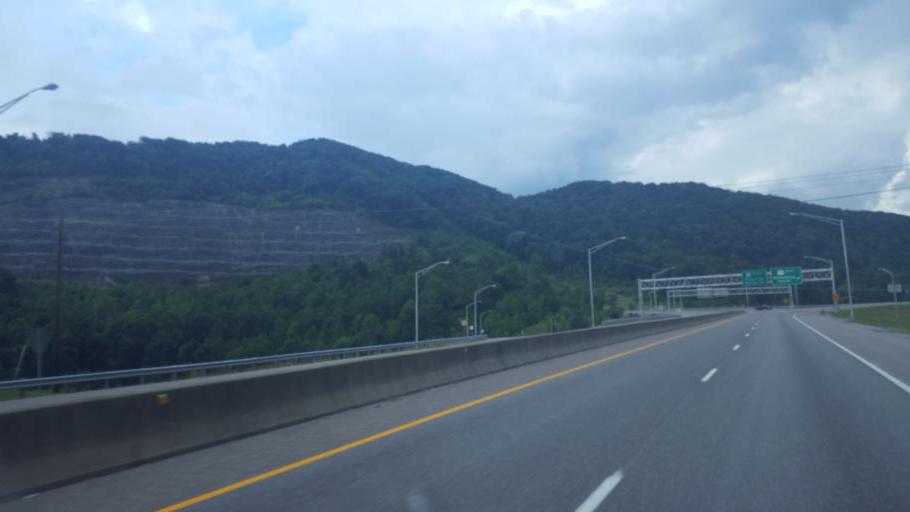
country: US
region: Kentucky
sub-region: Letcher County
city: Jenkins
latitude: 37.1620
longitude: -82.6478
